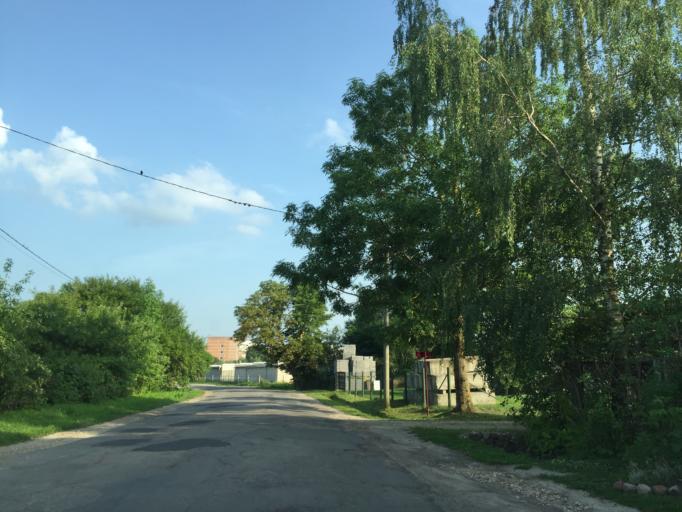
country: LV
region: Jelgava
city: Jelgava
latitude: 56.6639
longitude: 23.7007
